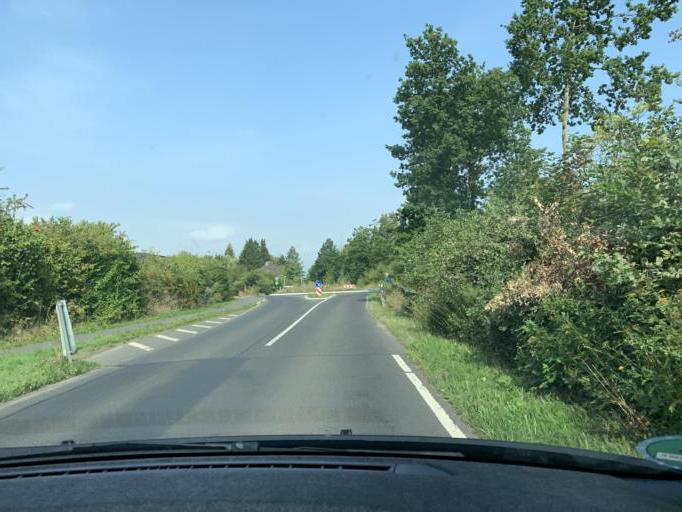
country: DE
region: North Rhine-Westphalia
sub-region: Regierungsbezirk Koln
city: Weilerswist
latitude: 50.8013
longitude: 6.8352
